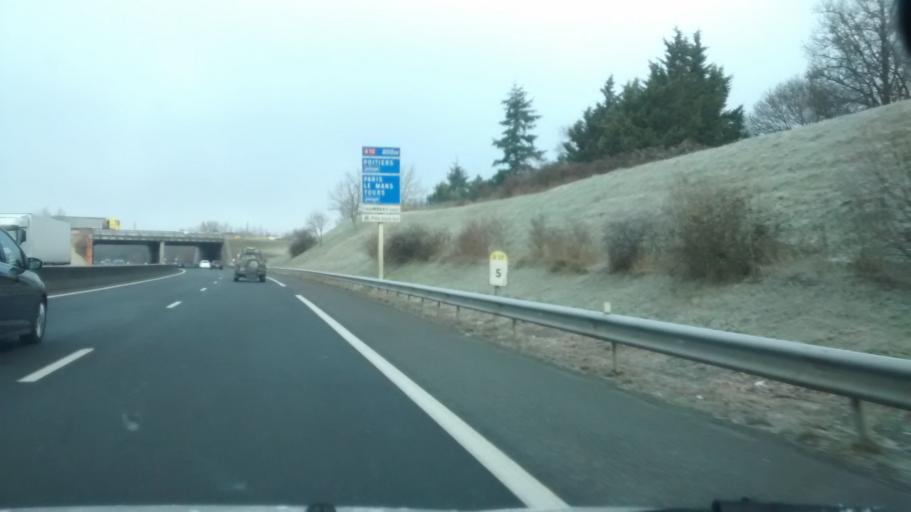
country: FR
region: Centre
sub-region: Departement d'Indre-et-Loire
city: Chambray-les-Tours
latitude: 47.3262
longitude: 0.6940
